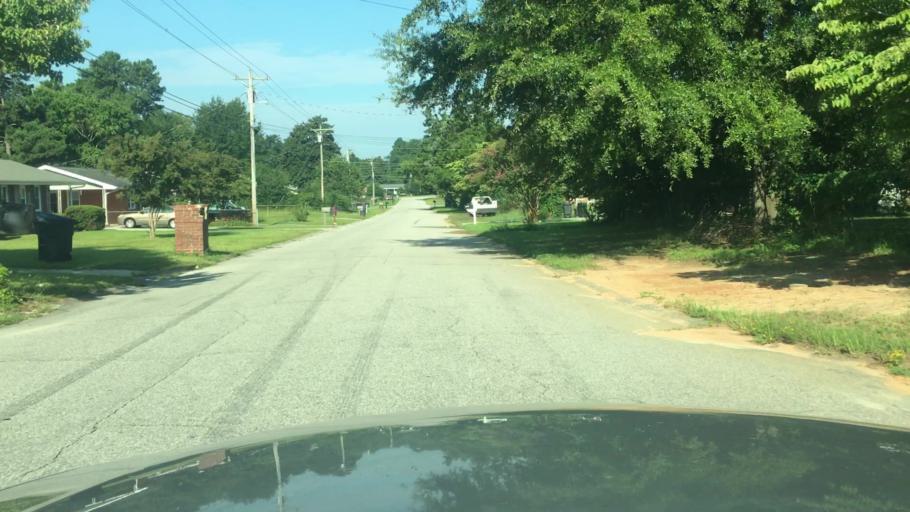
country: US
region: North Carolina
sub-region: Cumberland County
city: Spring Lake
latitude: 35.1534
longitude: -78.9161
